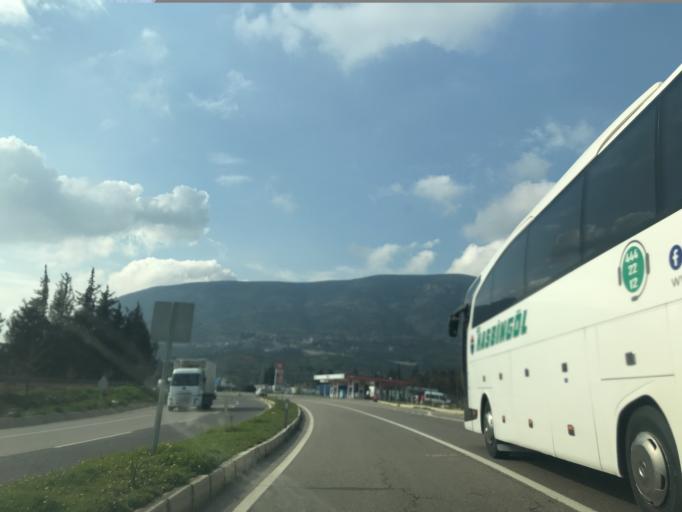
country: TR
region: Hatay
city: Kirikhan
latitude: 36.4771
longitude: 36.2875
